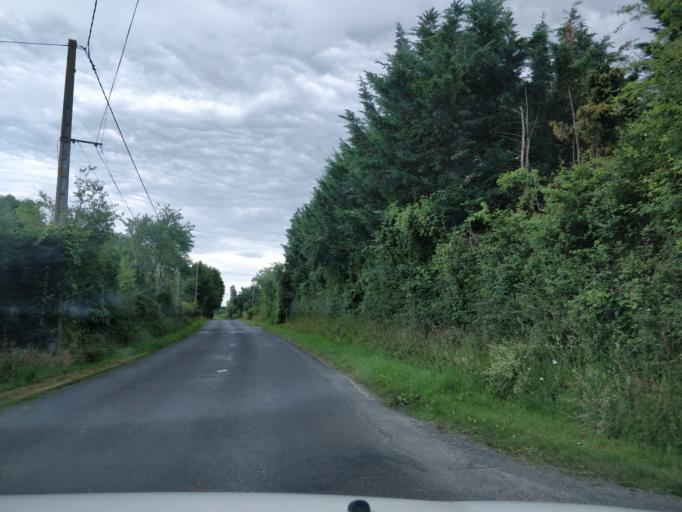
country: FR
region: Pays de la Loire
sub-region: Departement de Maine-et-Loire
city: Grez-Neuville
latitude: 47.6301
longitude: -0.6264
